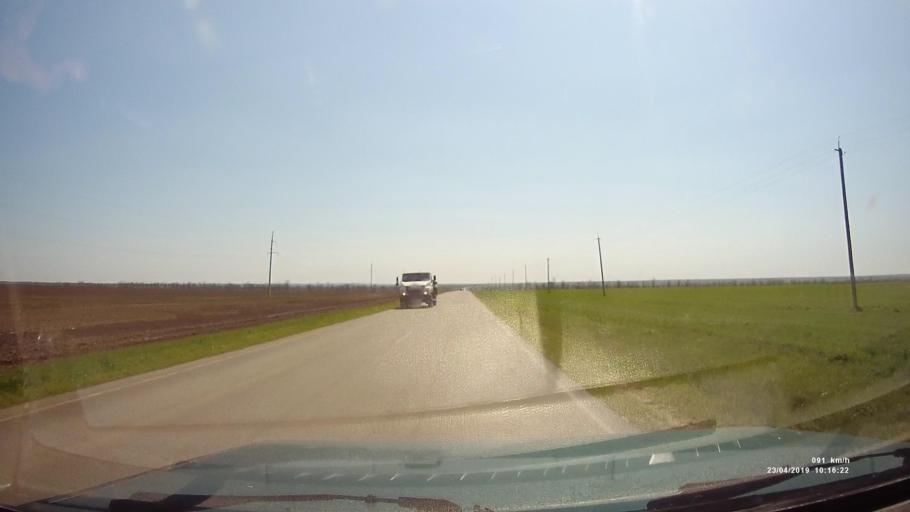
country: RU
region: Rostov
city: Sovetskoye
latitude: 46.6590
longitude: 42.3943
